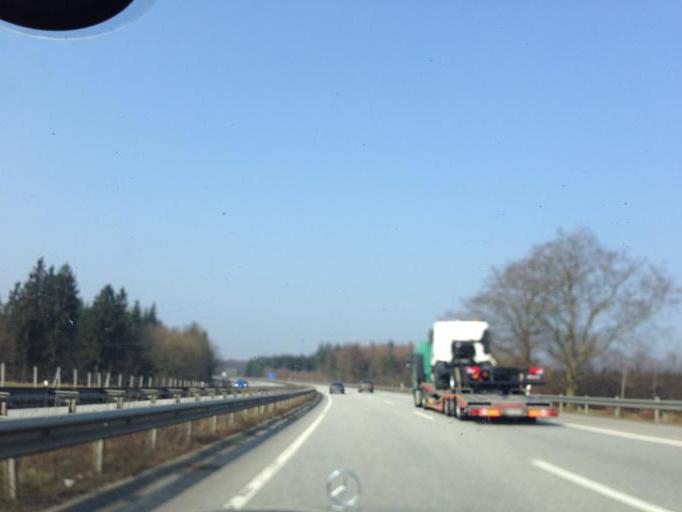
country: DE
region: Schleswig-Holstein
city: Daldorf
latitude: 54.0257
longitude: 10.2455
